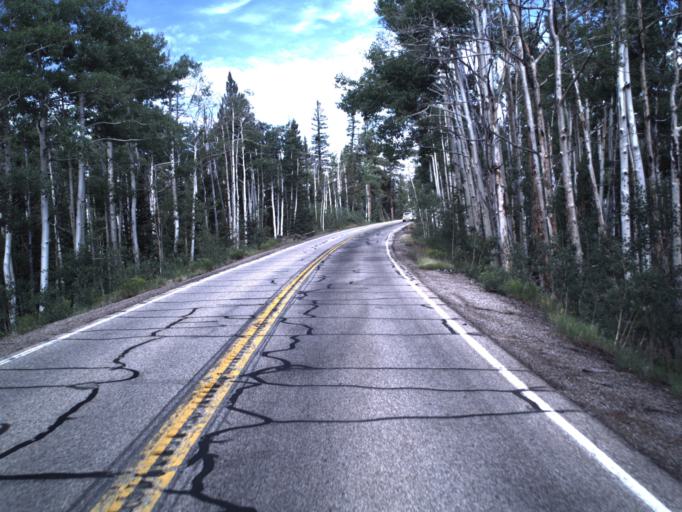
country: US
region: Utah
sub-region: Iron County
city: Parowan
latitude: 37.5185
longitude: -112.7227
